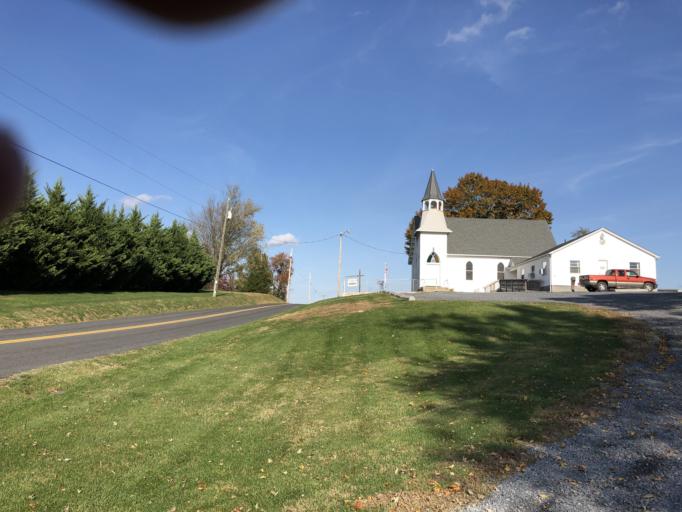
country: US
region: Virginia
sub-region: Frederick County
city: Shawnee Land
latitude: 39.1272
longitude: -78.2975
